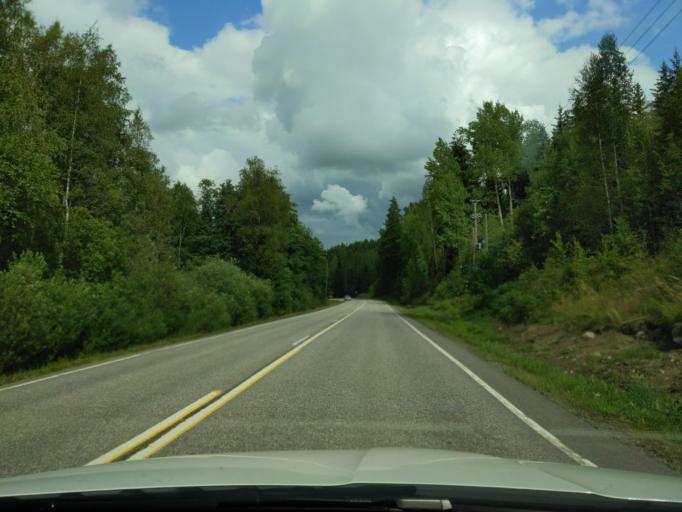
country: FI
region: Uusimaa
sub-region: Porvoo
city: Porvoo
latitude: 60.4433
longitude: 25.7289
